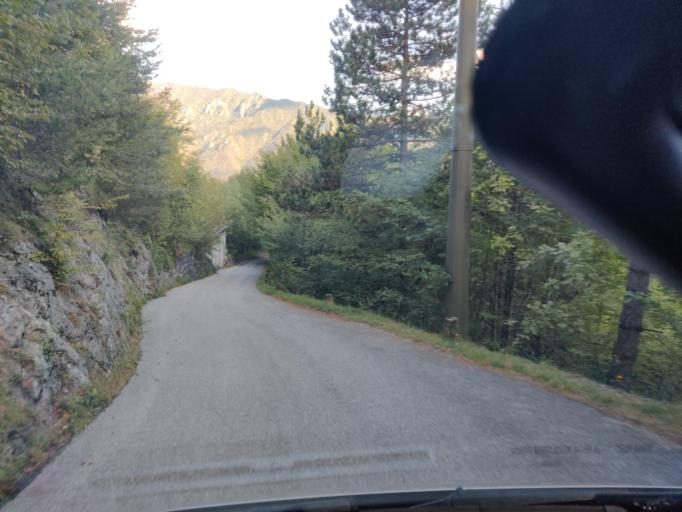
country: IT
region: Lombardy
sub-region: Provincia di Brescia
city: Anfo
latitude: 45.7695
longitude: 10.4888
